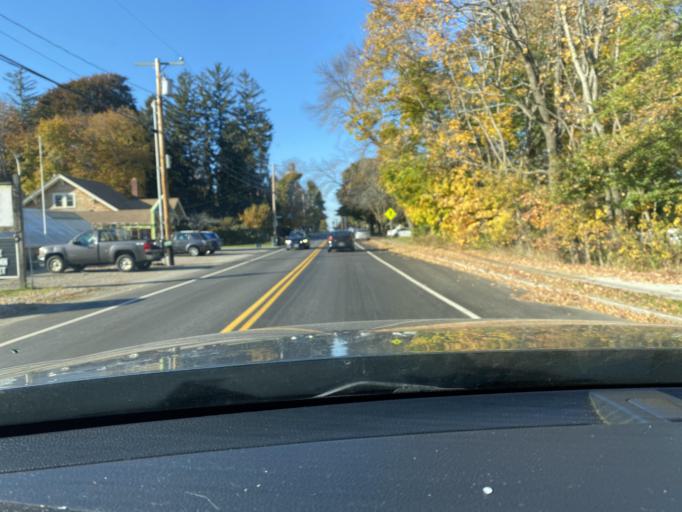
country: US
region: New Hampshire
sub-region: Rockingham County
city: Portsmouth
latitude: 43.0816
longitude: -70.7843
